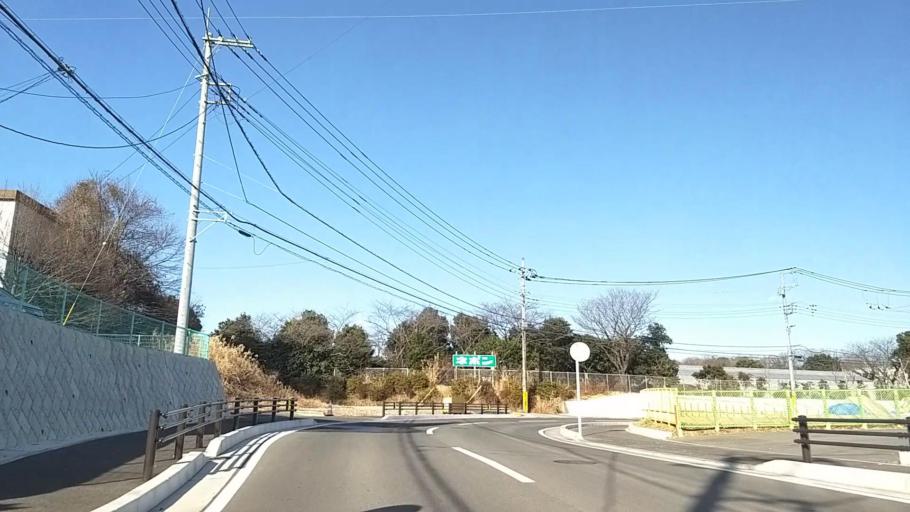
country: JP
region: Kanagawa
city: Atsugi
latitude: 35.4505
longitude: 139.3112
